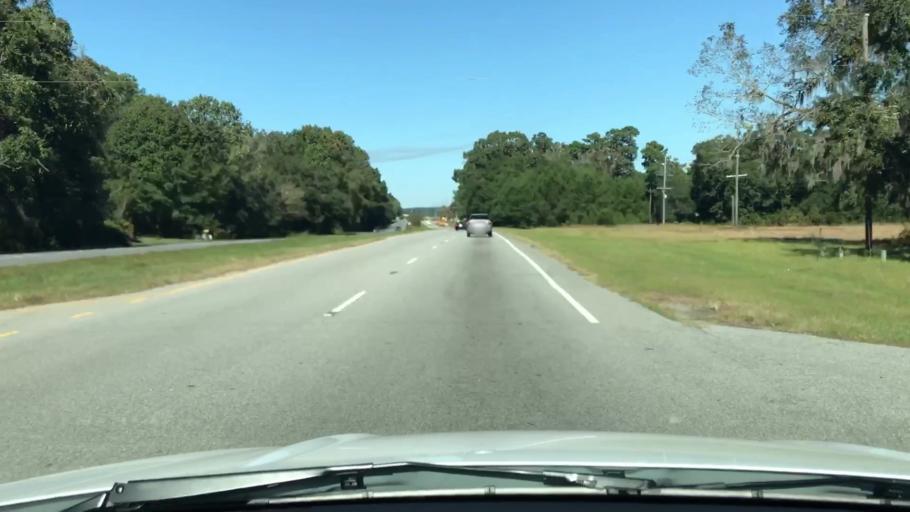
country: US
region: South Carolina
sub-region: Beaufort County
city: Laurel Bay
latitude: 32.5261
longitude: -80.7489
